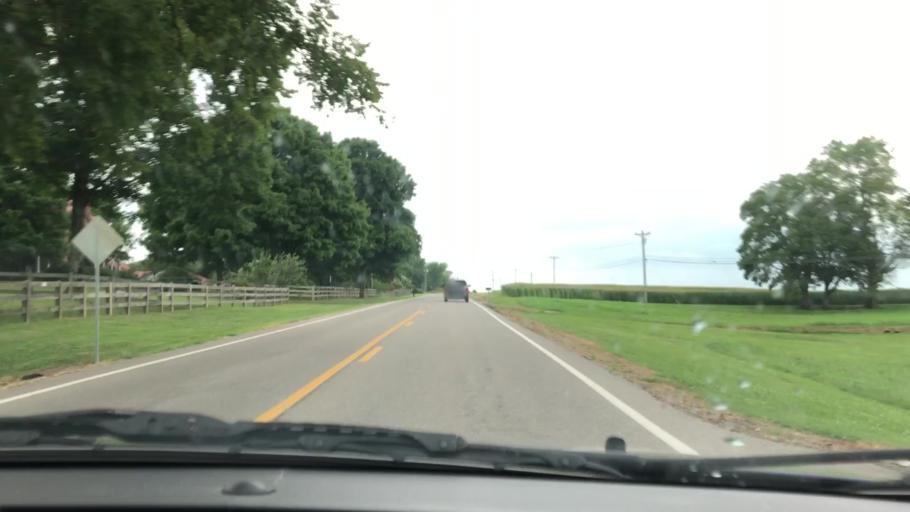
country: US
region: Tennessee
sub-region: Maury County
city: Columbia
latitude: 35.7055
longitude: -87.0157
